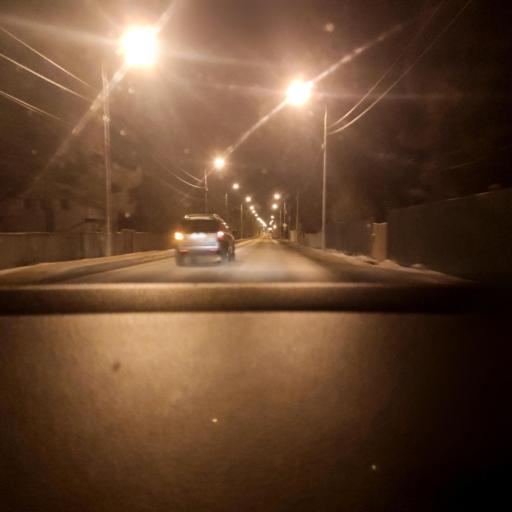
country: RU
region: Moskovskaya
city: Zhavoronki
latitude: 55.6480
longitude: 37.1008
